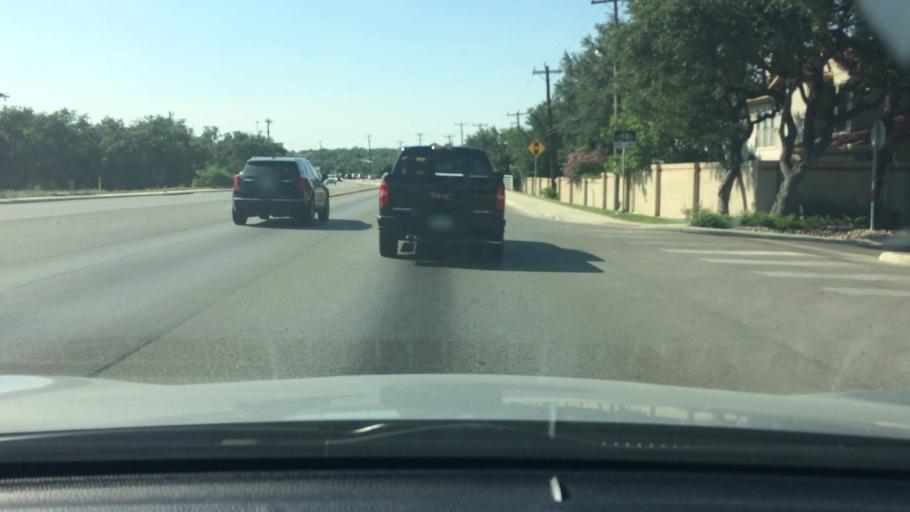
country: US
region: Texas
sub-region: Bexar County
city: Hollywood Park
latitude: 29.6190
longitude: -98.5112
